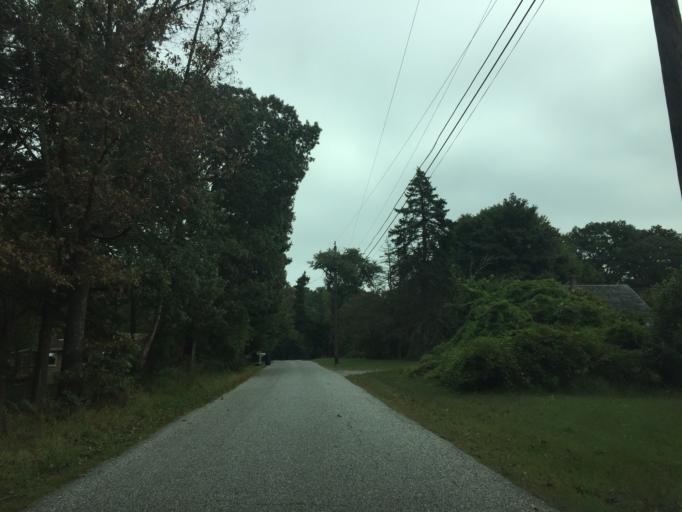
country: US
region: Maryland
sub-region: Baltimore County
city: Bowleys Quarters
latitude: 39.3741
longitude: -76.3879
